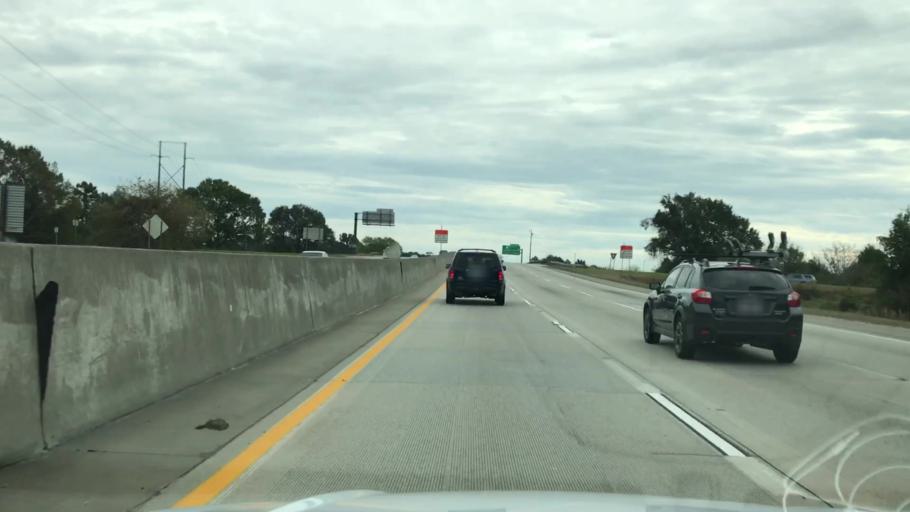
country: US
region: South Carolina
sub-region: Charleston County
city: North Charleston
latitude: 32.8443
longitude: -79.9829
